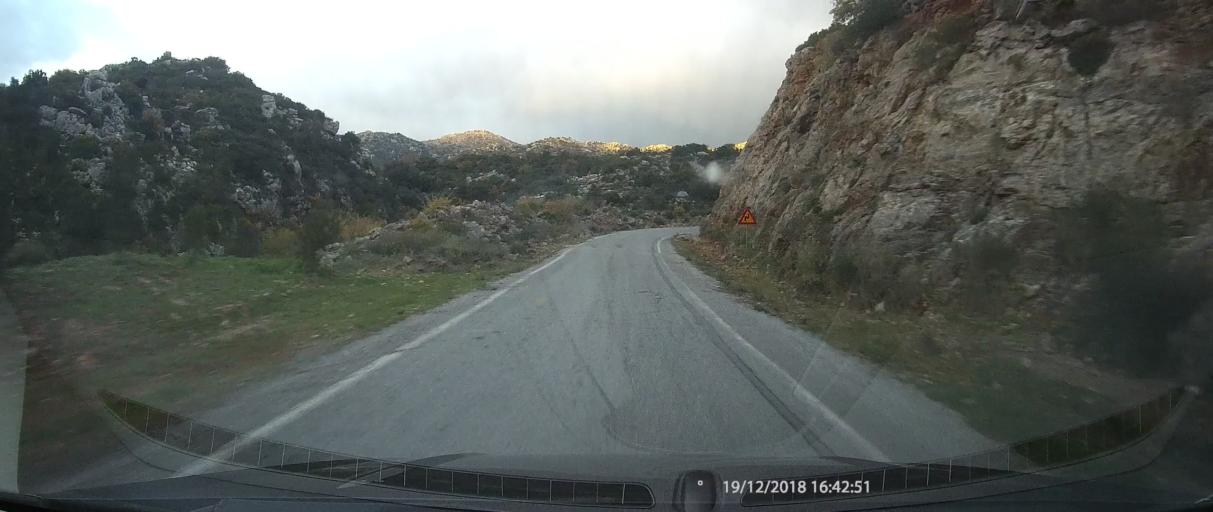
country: GR
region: Peloponnese
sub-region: Nomos Lakonias
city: Sykea
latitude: 36.9090
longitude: 22.9960
